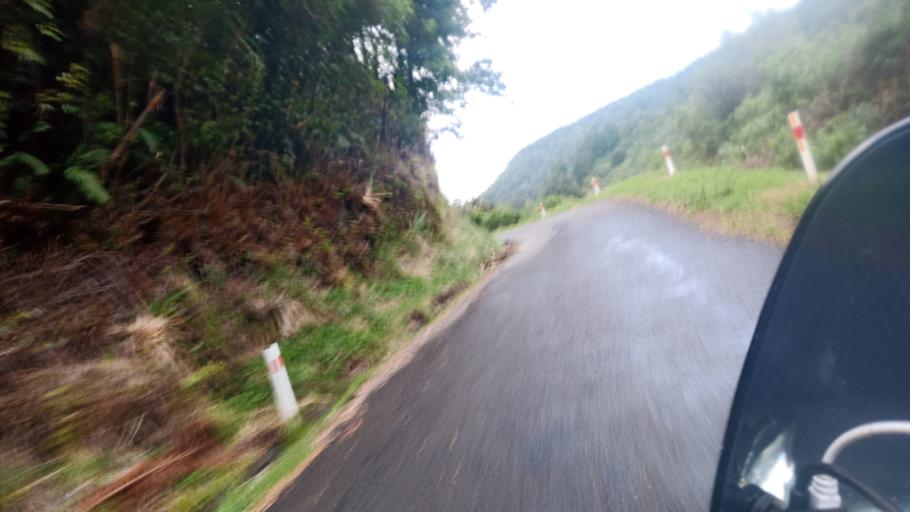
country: NZ
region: Hawke's Bay
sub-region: Wairoa District
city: Wairoa
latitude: -38.7306
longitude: 177.0962
